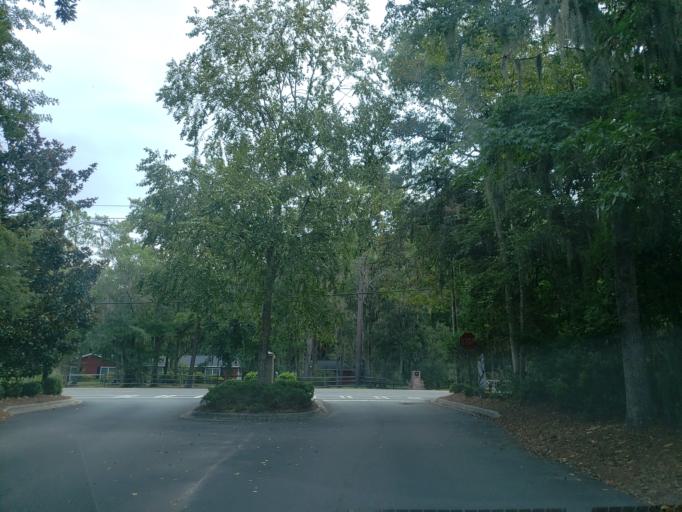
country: US
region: Georgia
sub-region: Chatham County
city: Wilmington Island
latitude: 32.0076
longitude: -80.9726
